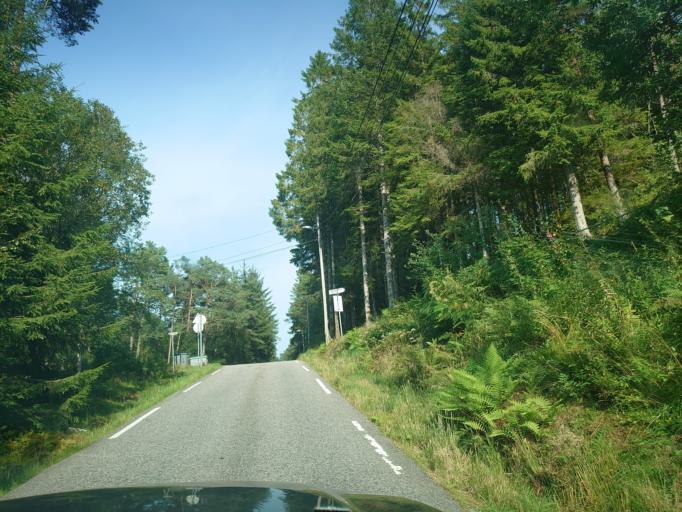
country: NO
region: Hordaland
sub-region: Bergen
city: Sandsli
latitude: 60.2707
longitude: 5.2729
